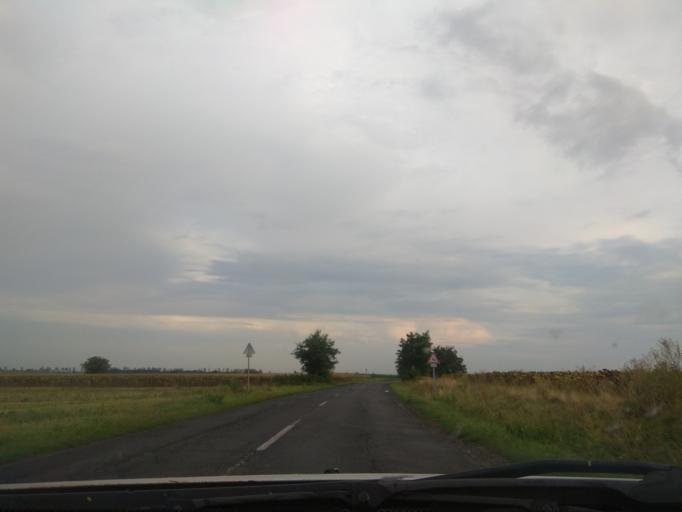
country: HU
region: Borsod-Abauj-Zemplen
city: Gesztely
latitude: 48.1219
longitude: 20.9734
